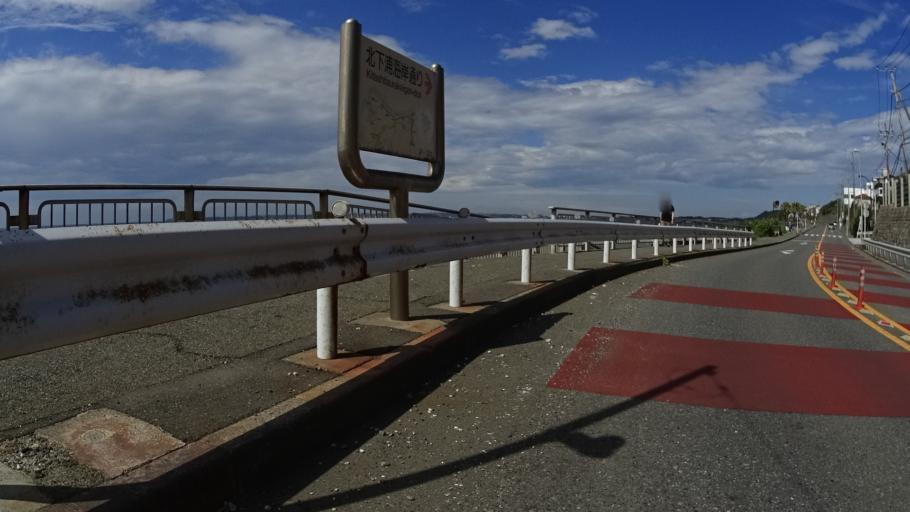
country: JP
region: Kanagawa
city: Yokosuka
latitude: 35.2114
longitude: 139.7106
